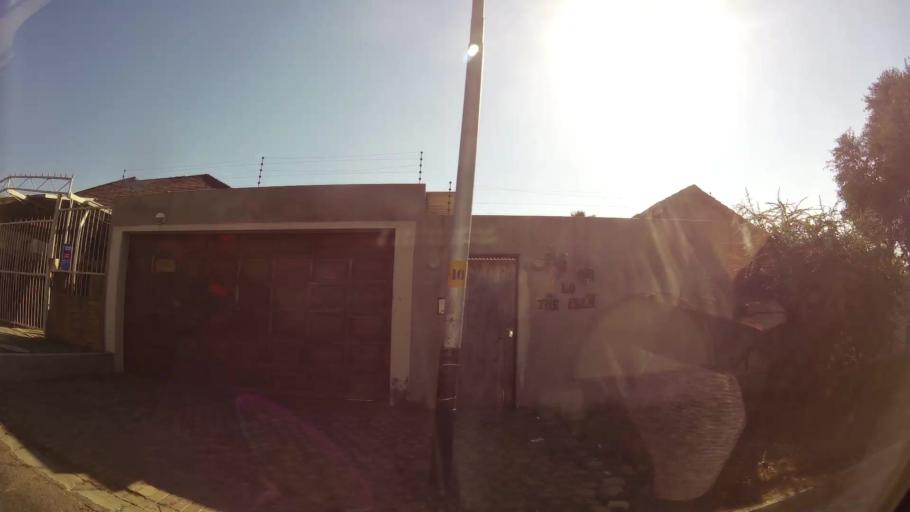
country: ZA
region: Gauteng
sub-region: Ekurhuleni Metropolitan Municipality
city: Germiston
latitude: -26.2554
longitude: 28.1090
